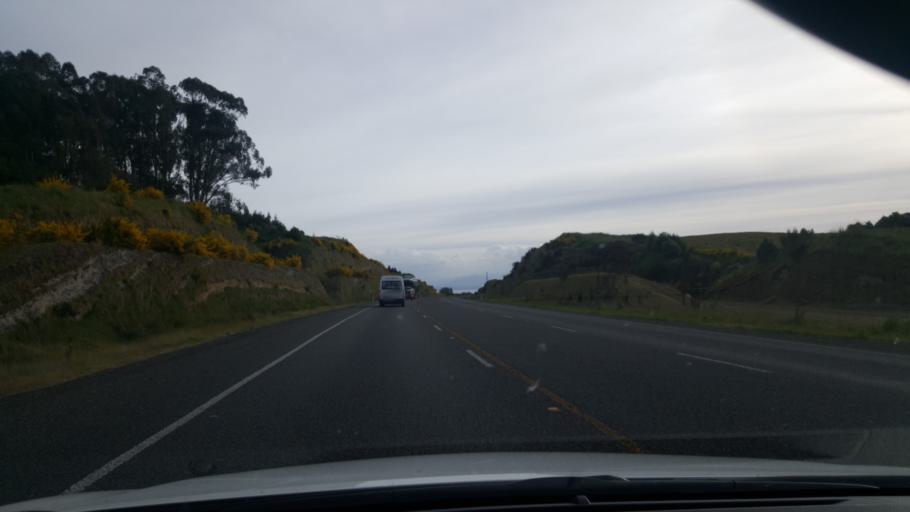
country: NZ
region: Waikato
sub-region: Taupo District
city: Taupo
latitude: -38.7117
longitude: 176.1093
